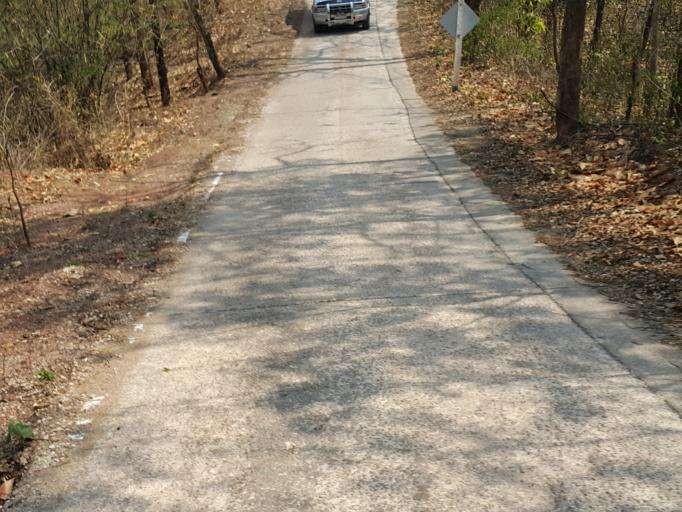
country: TH
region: Lampang
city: Mueang Pan
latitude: 18.7511
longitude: 99.5394
